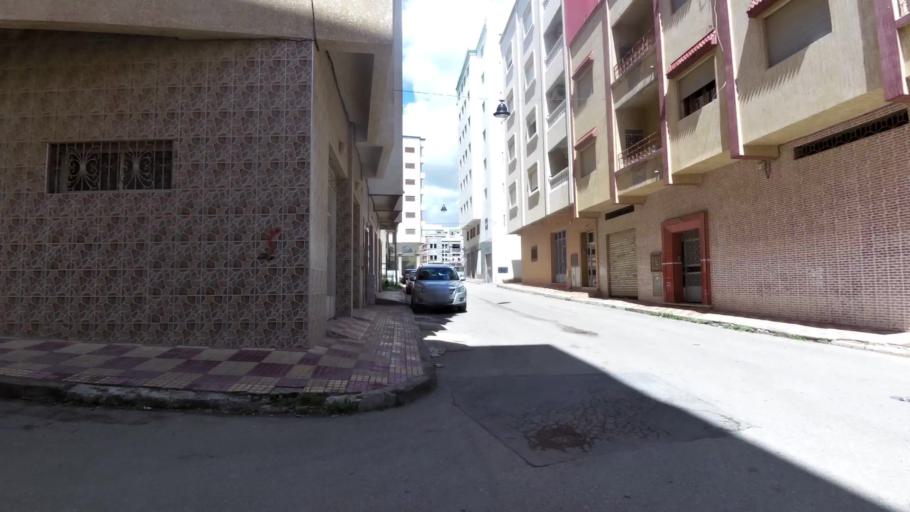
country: MA
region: Tanger-Tetouan
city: Tetouan
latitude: 35.5837
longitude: -5.3412
